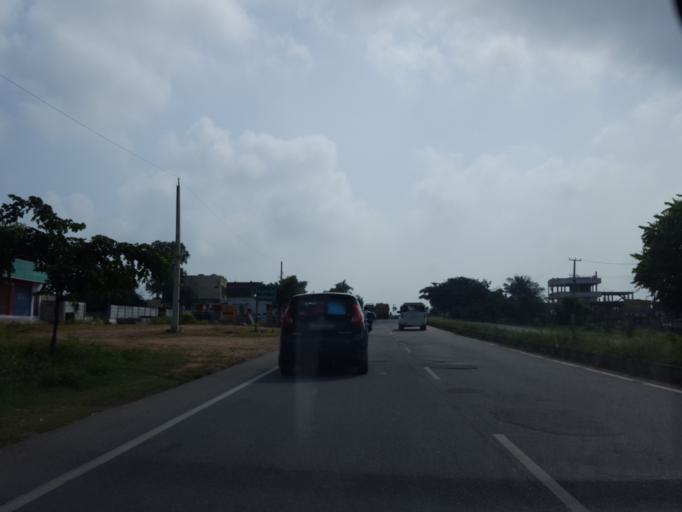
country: IN
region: Telangana
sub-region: Rangareddi
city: Ghatkesar
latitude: 17.2919
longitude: 78.7585
